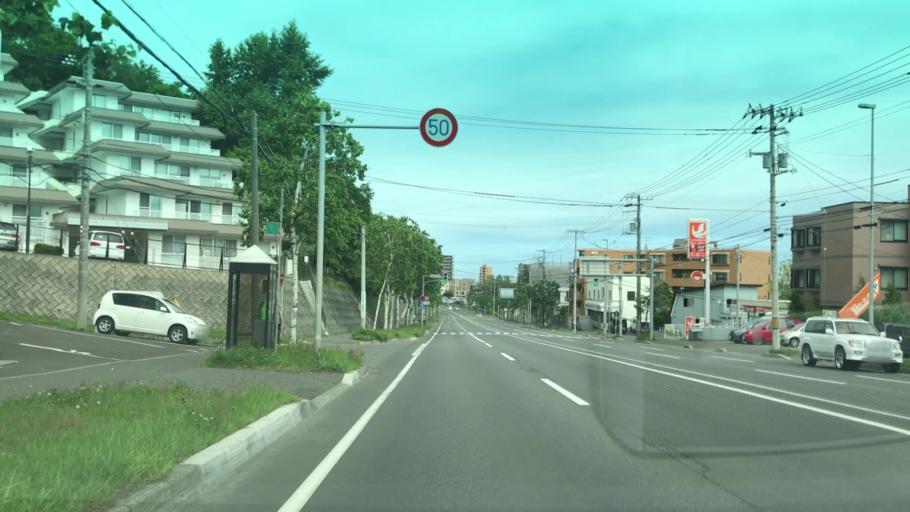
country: JP
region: Hokkaido
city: Sapporo
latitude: 43.0664
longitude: 141.2885
